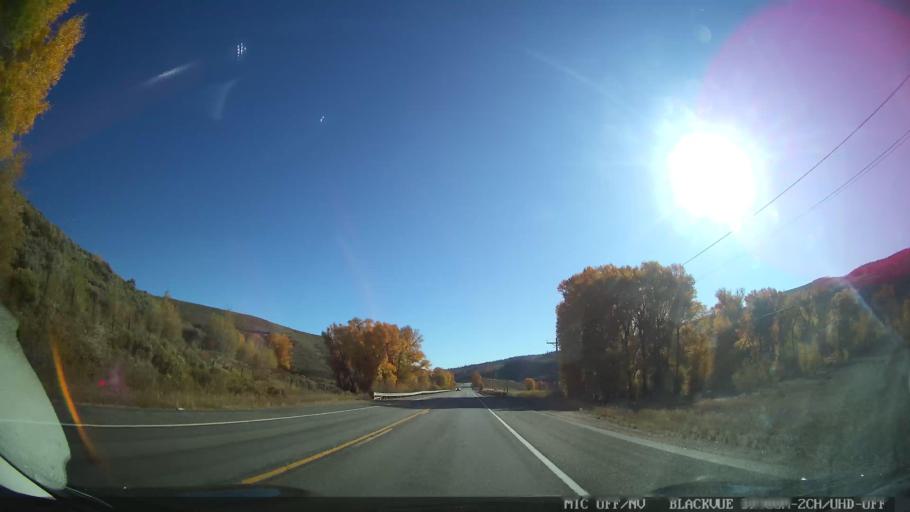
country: US
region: Colorado
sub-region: Grand County
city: Hot Sulphur Springs
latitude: 40.0986
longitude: -106.0404
